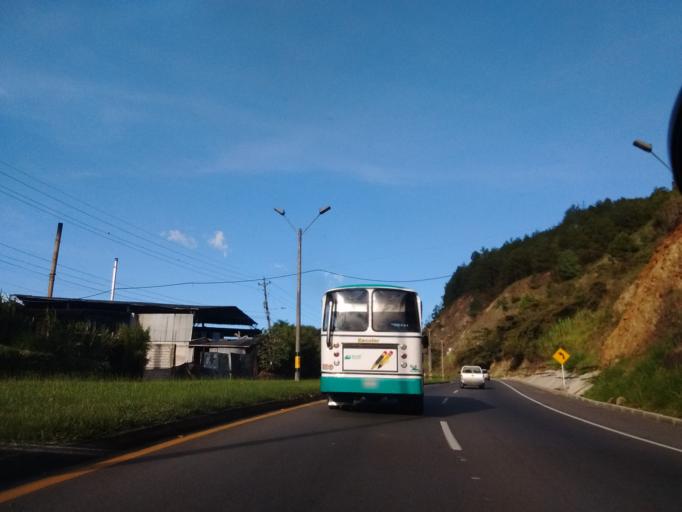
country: CO
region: Antioquia
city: Bello
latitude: 6.3232
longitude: -75.5420
